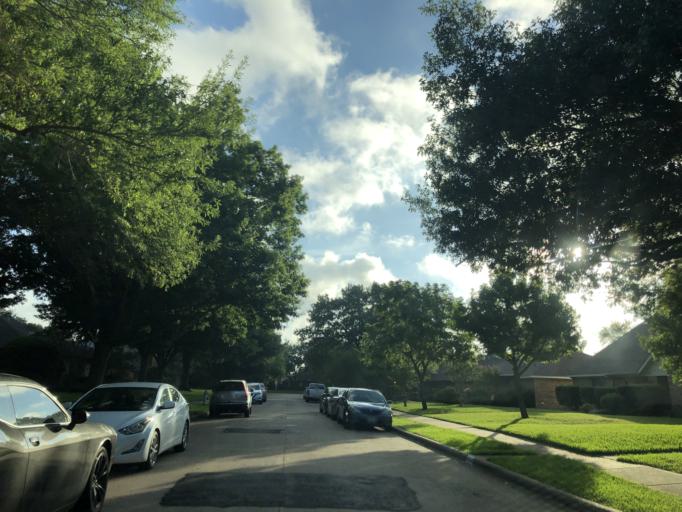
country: US
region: Texas
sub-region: Dallas County
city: Garland
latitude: 32.8461
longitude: -96.6278
